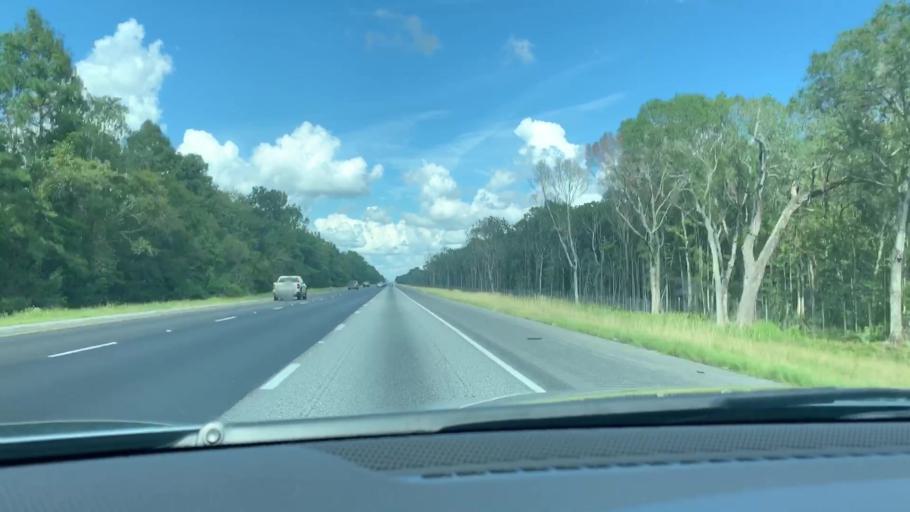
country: US
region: Georgia
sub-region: Camden County
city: Woodbine
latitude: 30.8887
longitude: -81.6857
